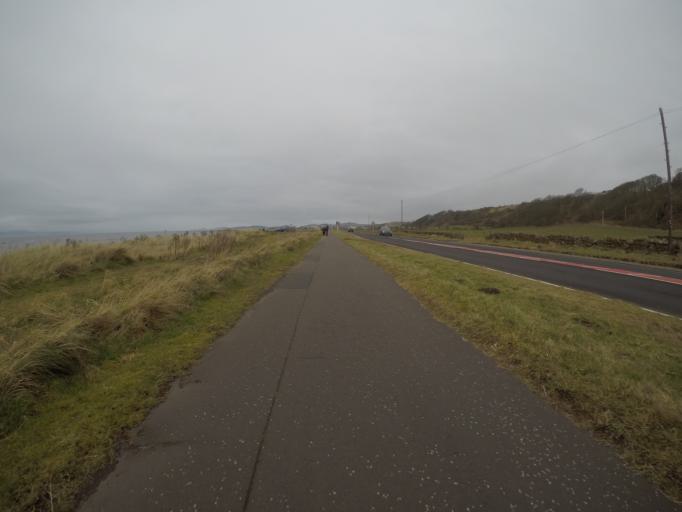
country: GB
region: Scotland
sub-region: North Ayrshire
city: West Kilbride
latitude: 55.6703
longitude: -4.8459
